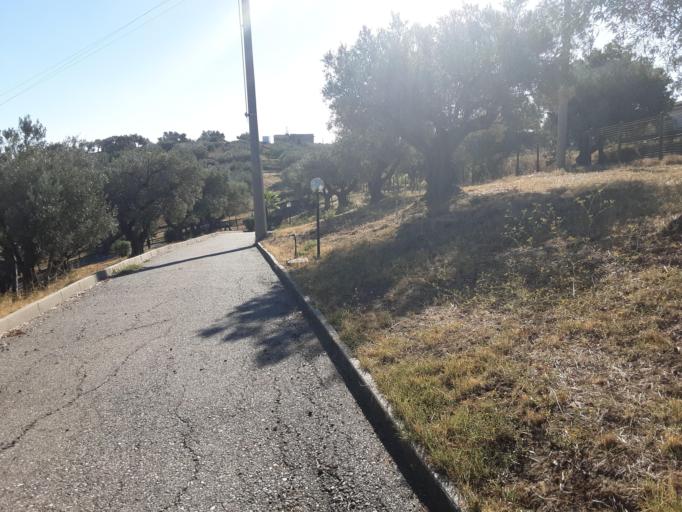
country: IT
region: Calabria
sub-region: Provincia di Catanzaro
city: Staletti
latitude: 38.7648
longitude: 16.5533
